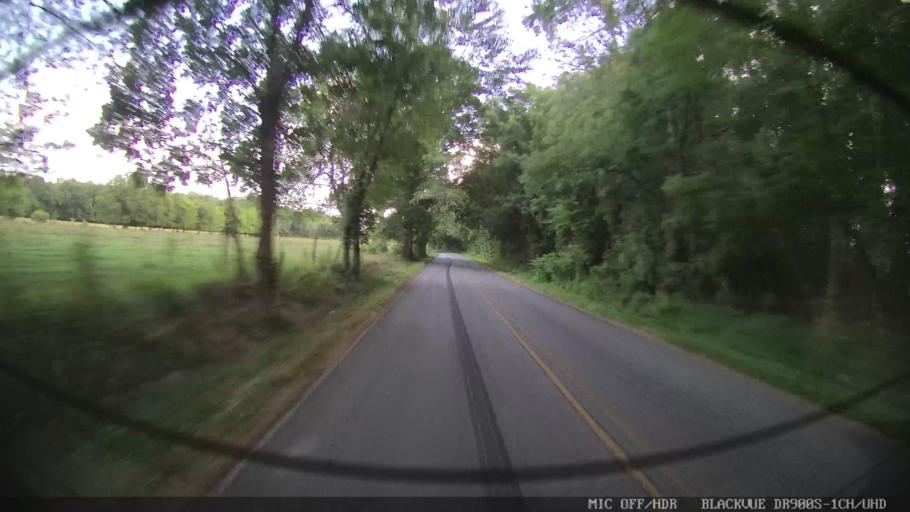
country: US
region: Georgia
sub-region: Bartow County
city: Rydal
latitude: 34.2753
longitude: -84.7994
